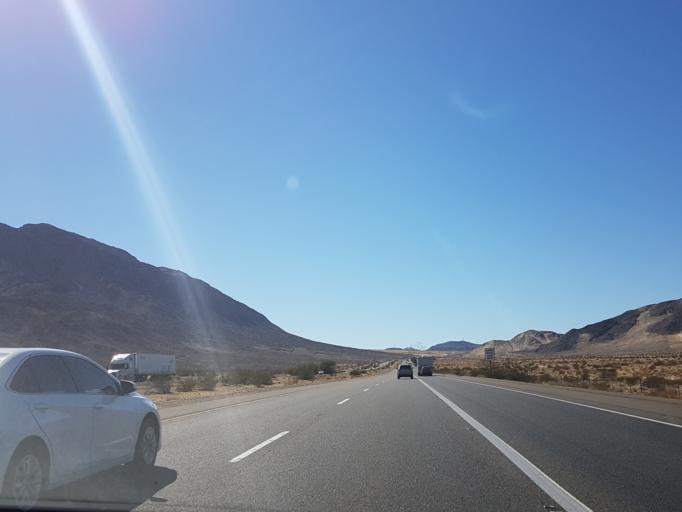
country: US
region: California
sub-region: San Bernardino County
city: Fort Irwin
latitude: 35.0962
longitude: -116.2993
